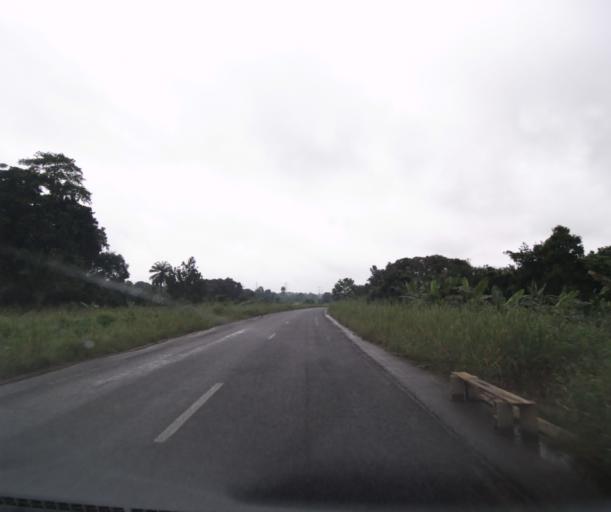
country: CM
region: Littoral
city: Edea
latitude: 3.4889
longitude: 10.1249
